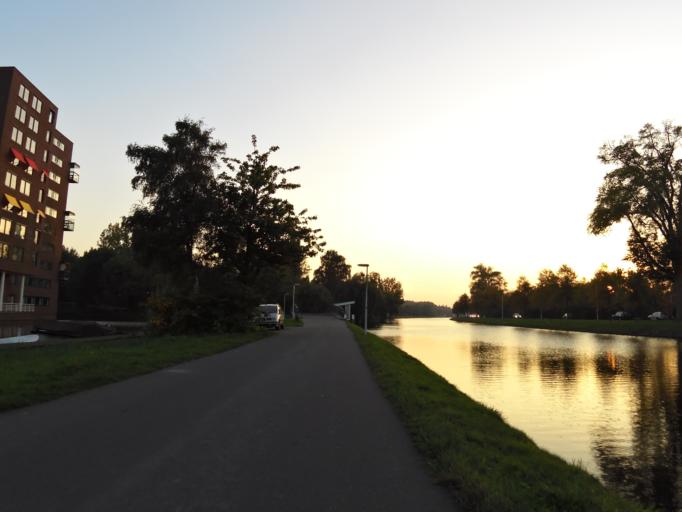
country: NL
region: South Holland
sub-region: Gemeente Leiden
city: Leiden
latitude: 52.1484
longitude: 4.5094
